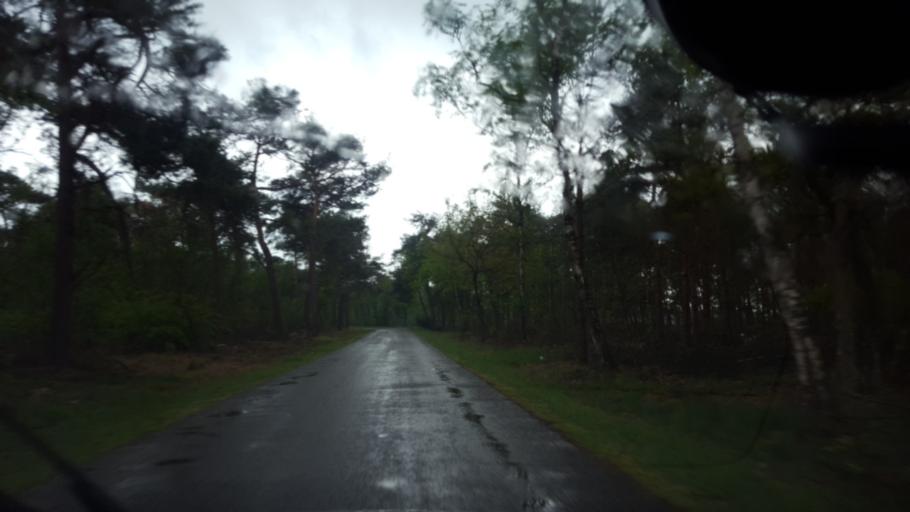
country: NL
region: North Brabant
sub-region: Gemeente Someren
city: Someren
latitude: 51.3891
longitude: 5.6646
